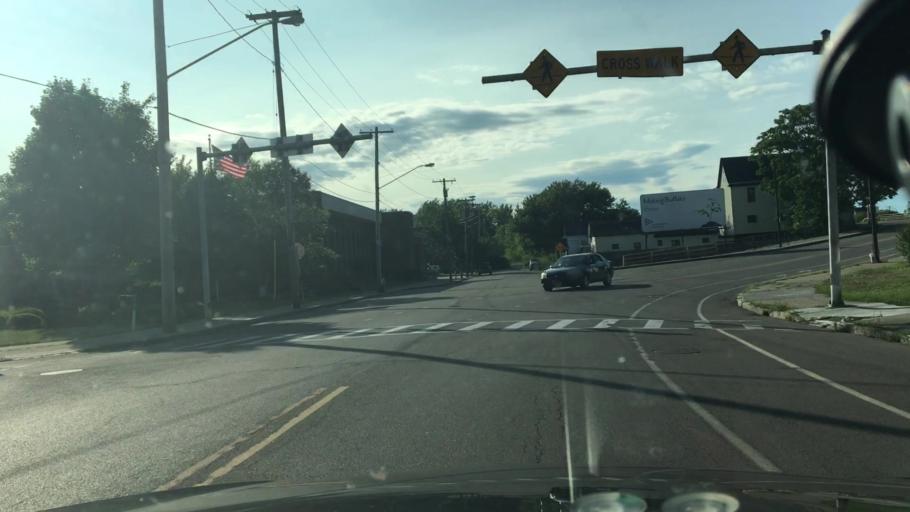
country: US
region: New York
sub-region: Erie County
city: Buffalo
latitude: 42.8676
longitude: -78.8503
